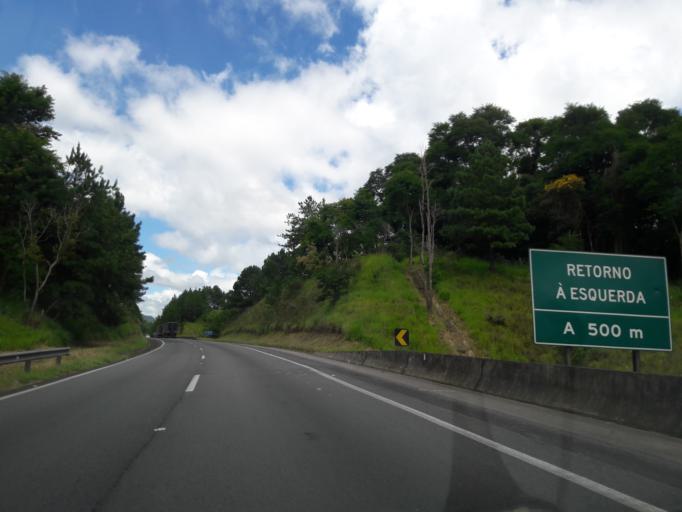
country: BR
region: Parana
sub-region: Campina Grande Do Sul
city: Campina Grande do Sul
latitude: -25.1114
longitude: -48.8533
